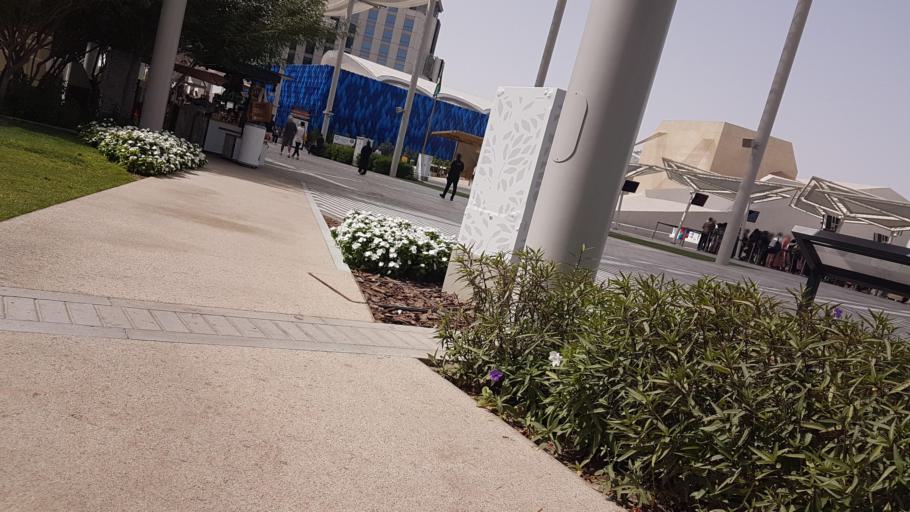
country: AE
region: Dubai
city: Dubai
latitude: 24.9632
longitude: 55.1507
